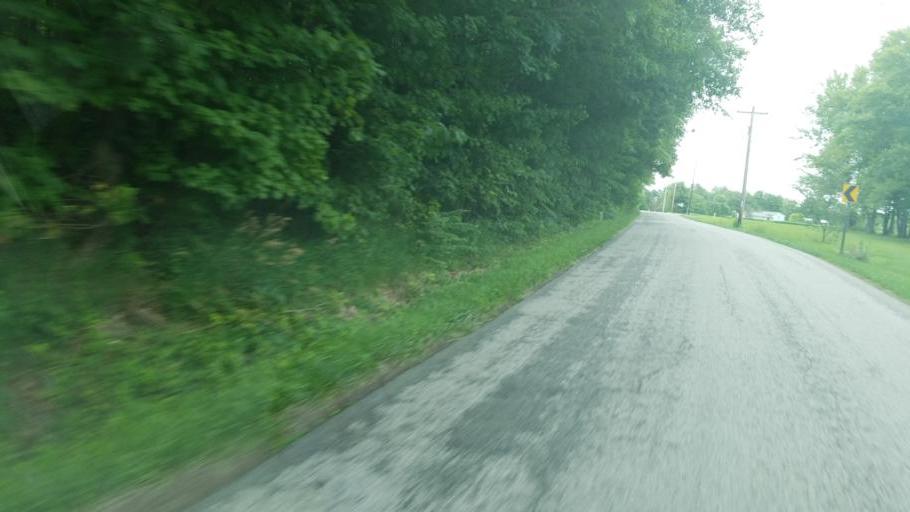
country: US
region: Ohio
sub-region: Delaware County
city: Ashley
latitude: 40.4208
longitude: -82.9965
